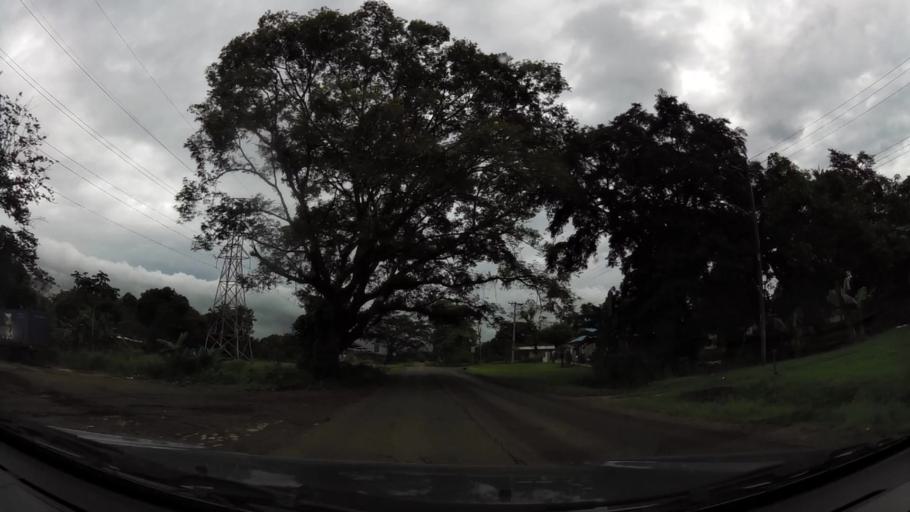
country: PA
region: Panama
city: Chilibre
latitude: 9.1428
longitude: -79.6162
